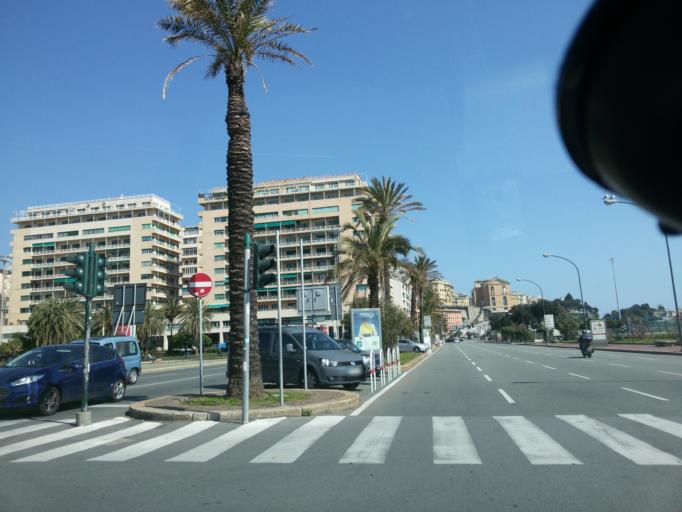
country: IT
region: Liguria
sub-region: Provincia di Genova
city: San Teodoro
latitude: 44.3961
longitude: 8.9449
